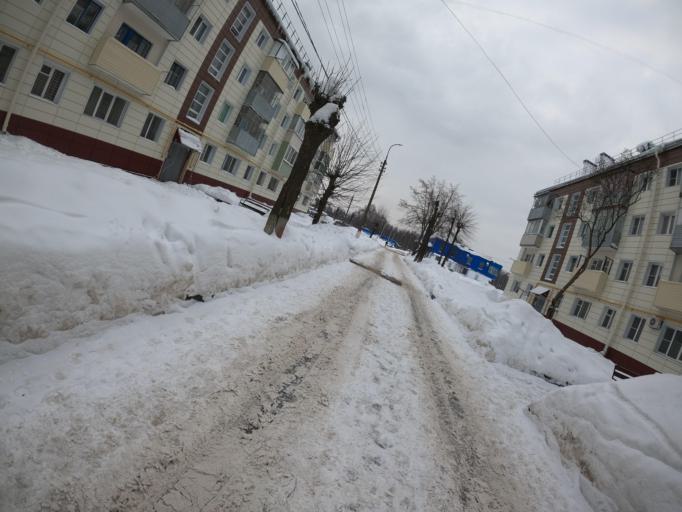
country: RU
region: Moskovskaya
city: Elektrogorsk
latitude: 55.8671
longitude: 38.7814
